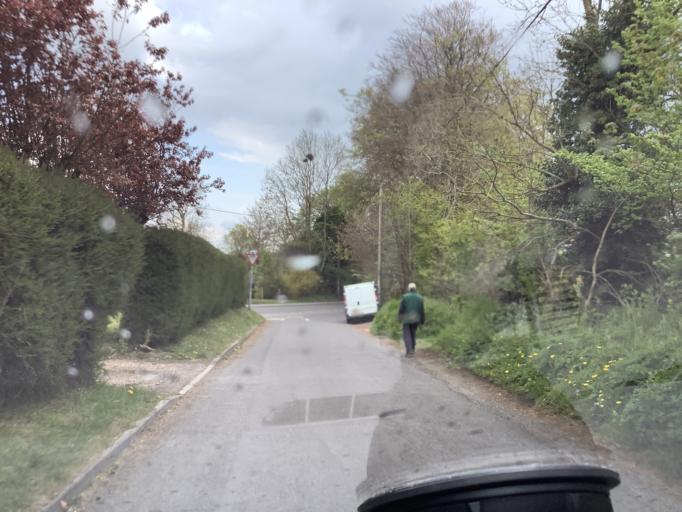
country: GB
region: England
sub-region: Wiltshire
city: Bratton
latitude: 51.2692
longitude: -2.1289
